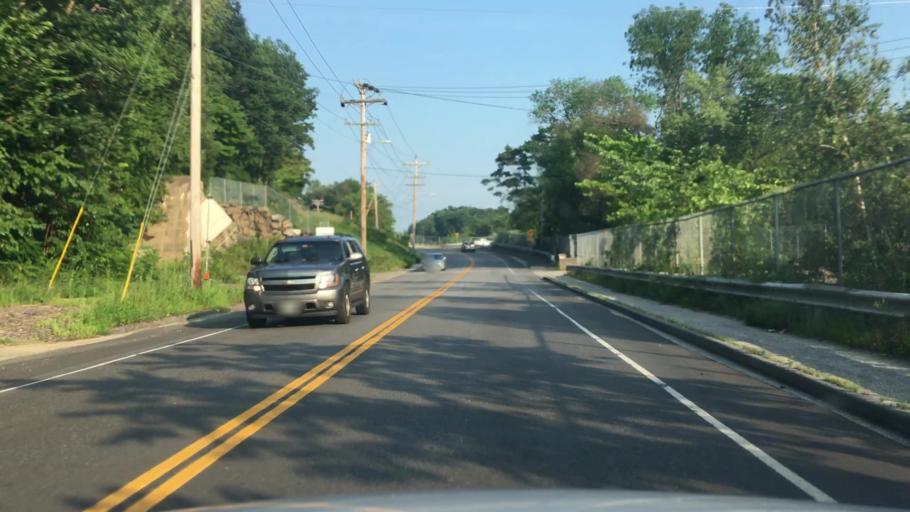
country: US
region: Maine
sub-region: Androscoggin County
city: Lisbon Falls
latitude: 43.9947
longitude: -70.0598
